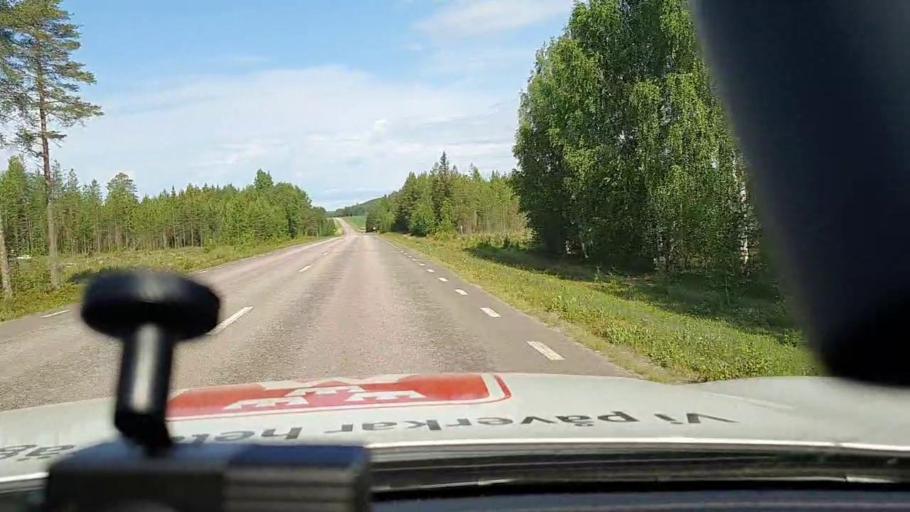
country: SE
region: Norrbotten
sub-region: Bodens Kommun
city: Boden
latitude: 65.9079
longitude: 21.3571
